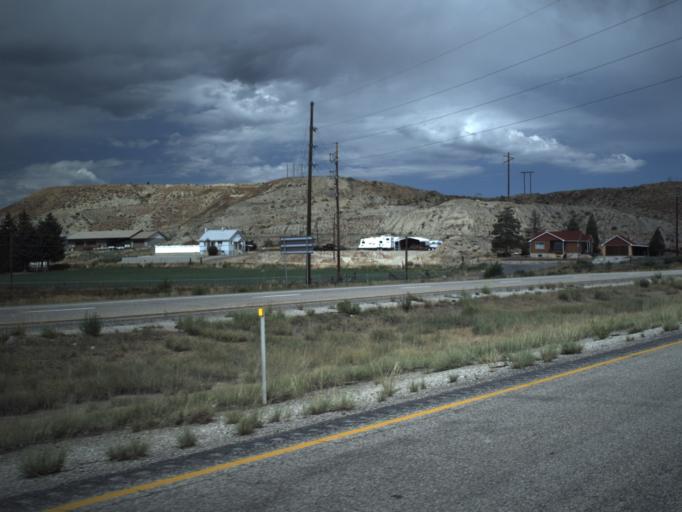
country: US
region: Utah
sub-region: Carbon County
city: Carbonville
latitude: 39.6083
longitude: -110.8331
